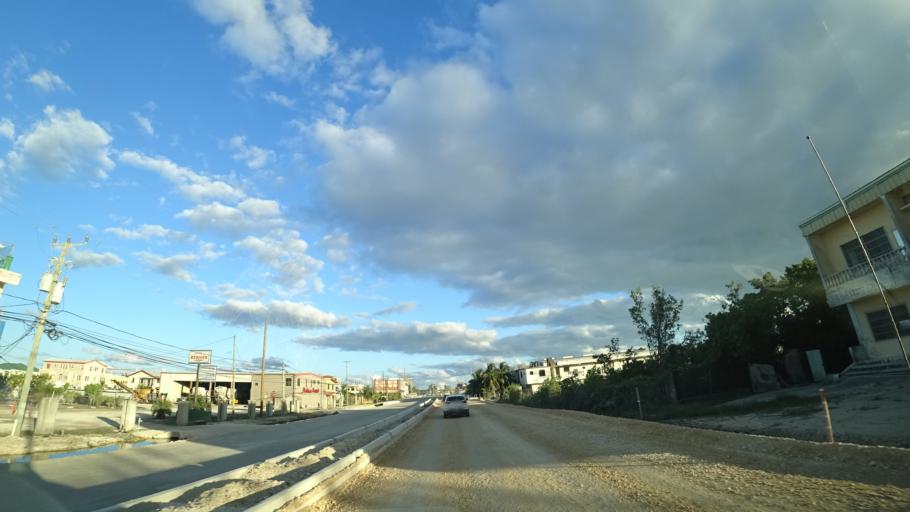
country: BZ
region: Belize
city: Belize City
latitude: 17.5171
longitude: -88.2295
